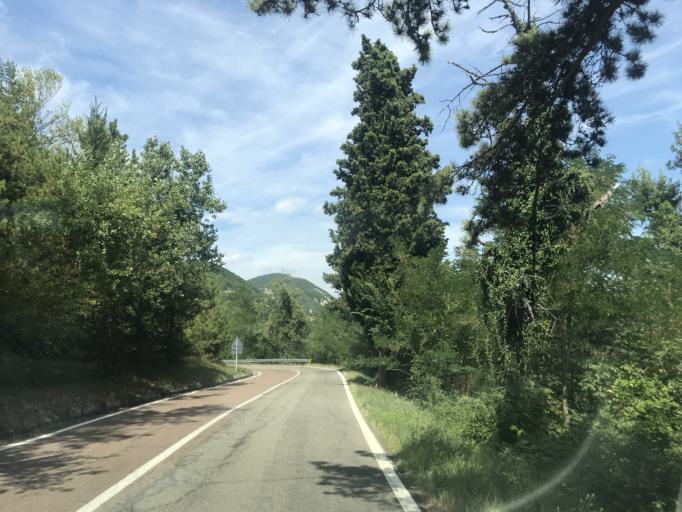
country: IT
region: Emilia-Romagna
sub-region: Provincia di Bologna
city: Grizzana
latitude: 44.2562
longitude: 11.1615
